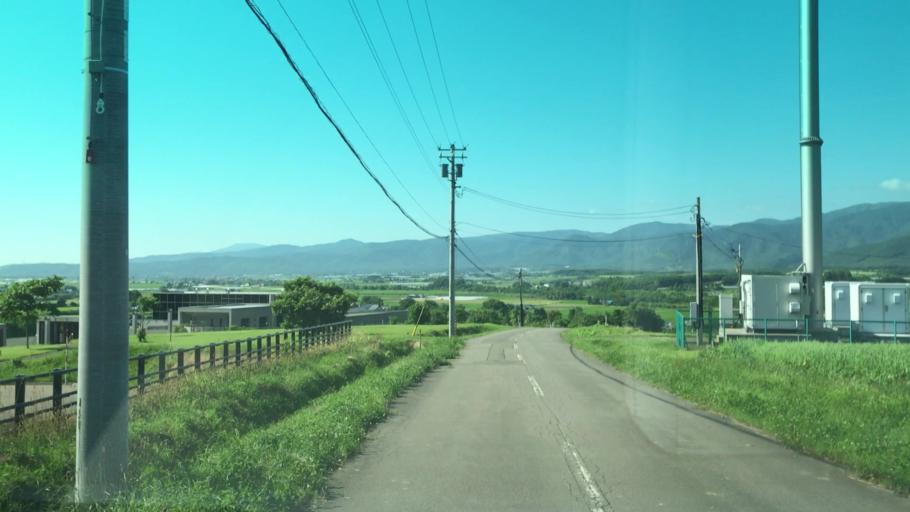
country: JP
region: Hokkaido
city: Iwanai
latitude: 42.9739
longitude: 140.6105
